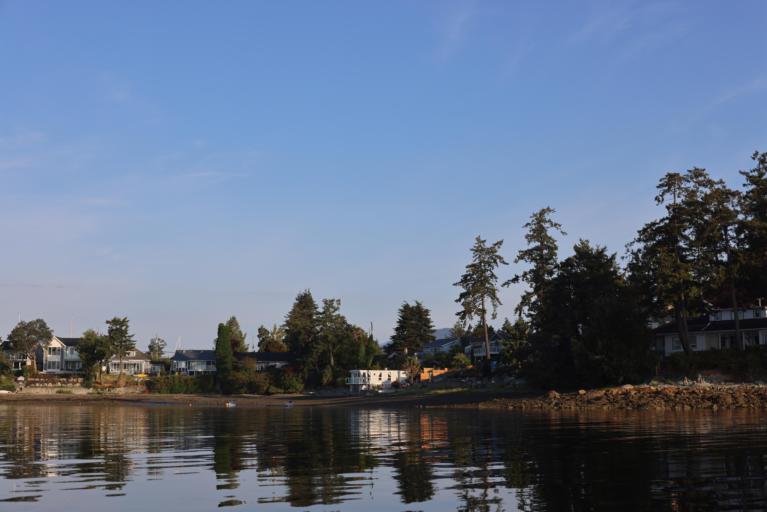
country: CA
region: British Columbia
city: North Saanich
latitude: 48.6645
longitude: -123.4003
